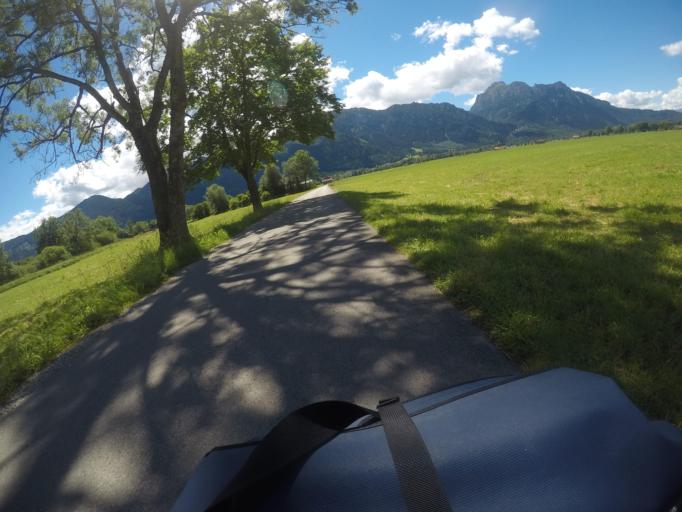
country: DE
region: Bavaria
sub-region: Swabia
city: Schwangau
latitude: 47.5890
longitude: 10.7471
